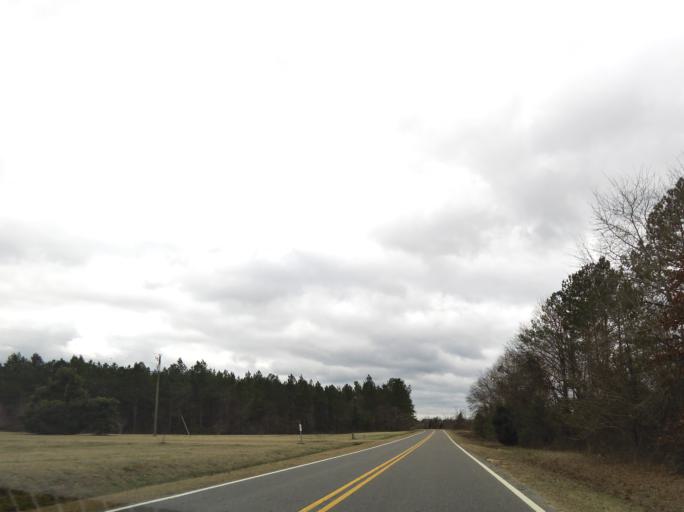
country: US
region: Georgia
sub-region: Bleckley County
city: Cochran
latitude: 32.4834
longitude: -83.3741
